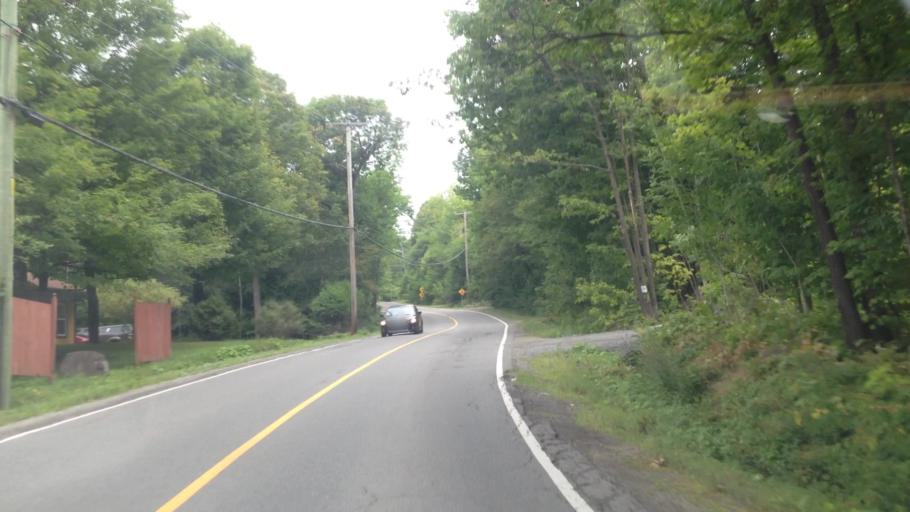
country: CA
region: Quebec
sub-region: Laurentides
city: Saint-Jerome
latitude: 45.8190
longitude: -73.9717
